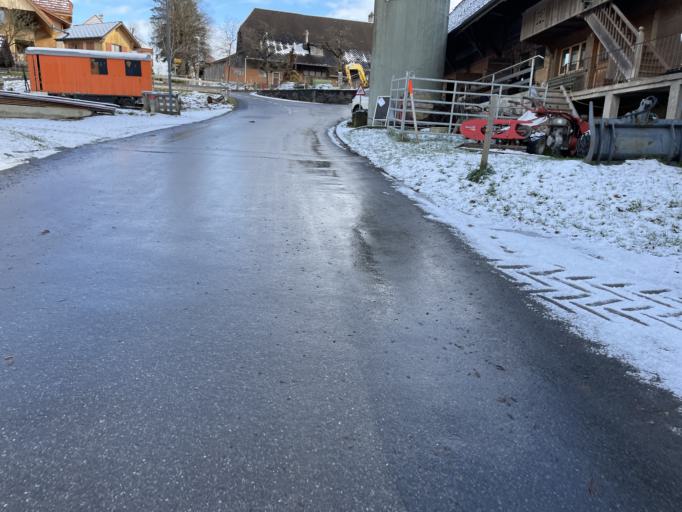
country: CH
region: Lucerne
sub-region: Entlebuch District
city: Oberdiessbach
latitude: 46.8576
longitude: 7.6047
